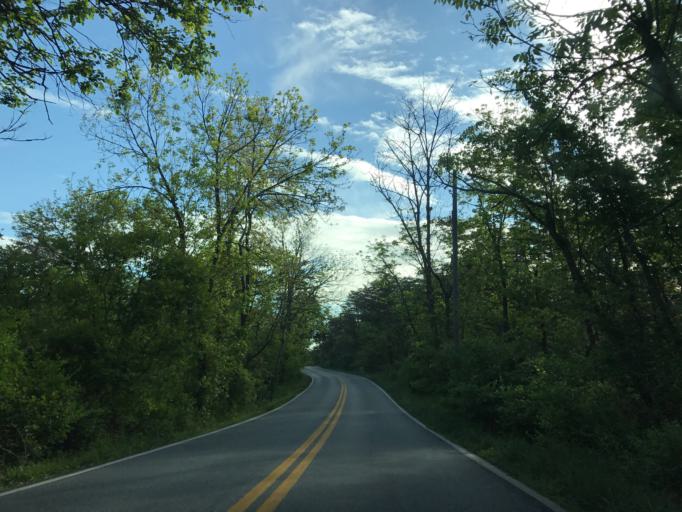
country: US
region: Maryland
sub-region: Baltimore County
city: Randallstown
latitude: 39.3996
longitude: -76.8258
